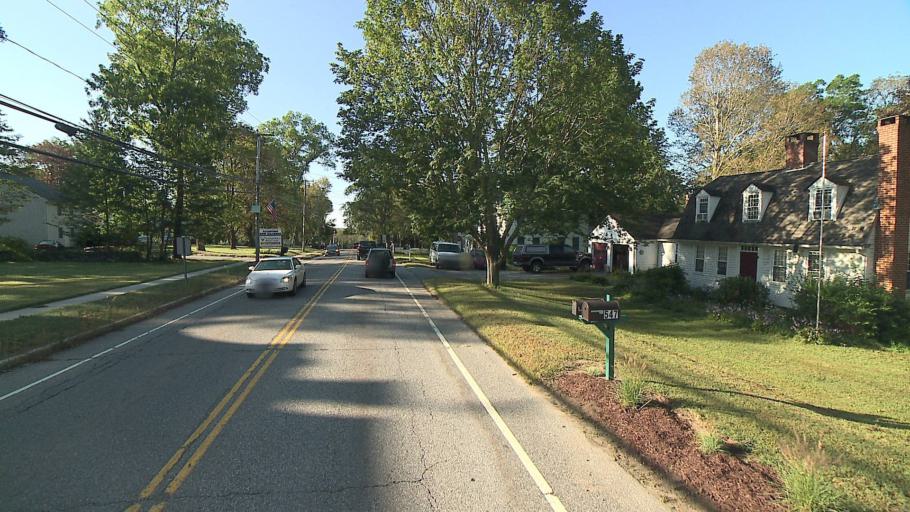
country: US
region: Connecticut
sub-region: Windham County
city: Plainfield
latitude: 41.6832
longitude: -71.9145
